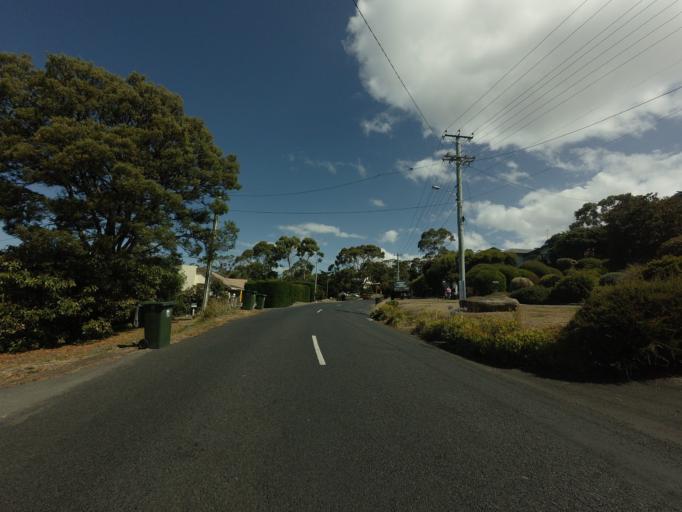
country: AU
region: Tasmania
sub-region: Hobart
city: Dynnyrne
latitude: -42.9167
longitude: 147.3241
